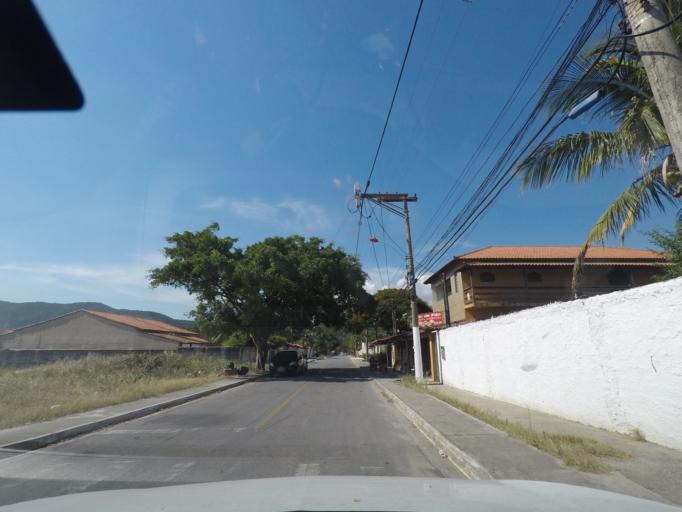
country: BR
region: Rio de Janeiro
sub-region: Niteroi
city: Niteroi
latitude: -22.9646
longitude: -42.9729
